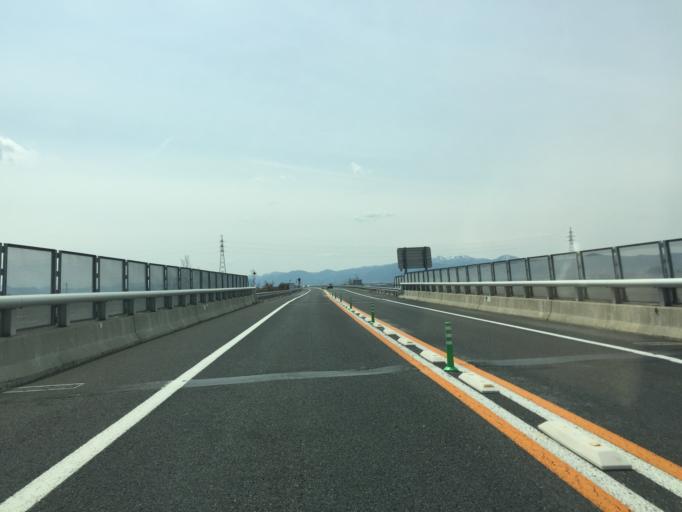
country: JP
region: Yamagata
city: Tendo
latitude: 38.3537
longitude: 140.3408
